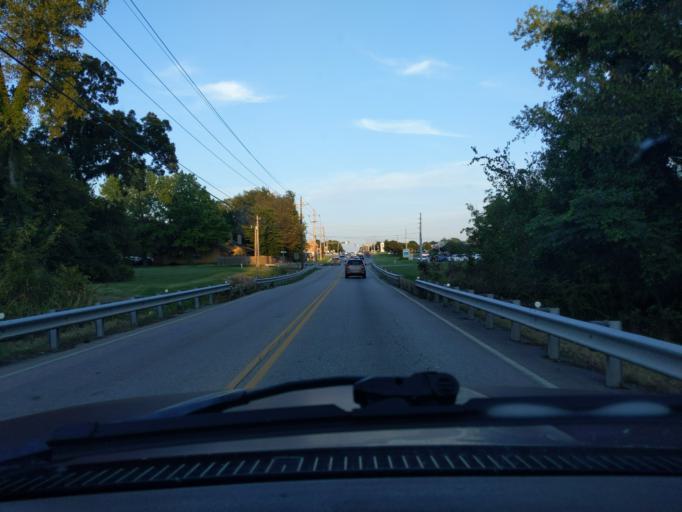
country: US
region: Oklahoma
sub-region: Tulsa County
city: Jenks
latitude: 36.0464
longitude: -95.8894
